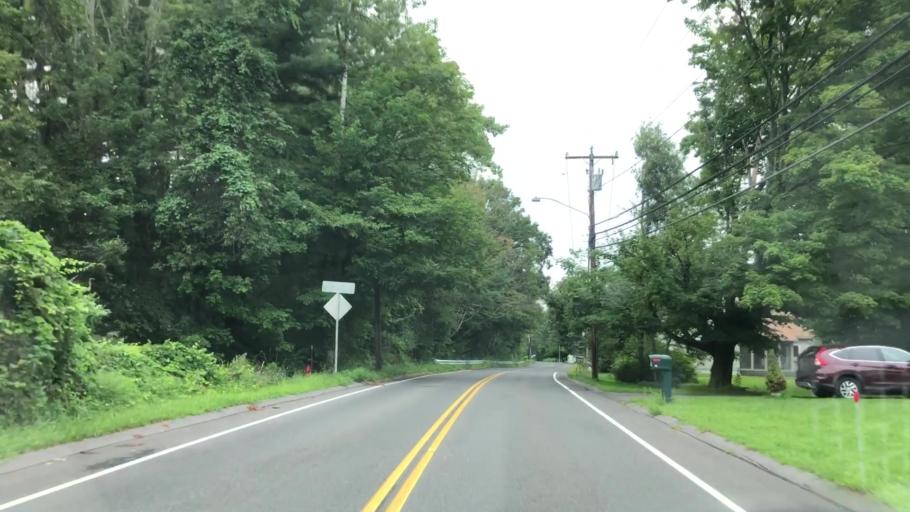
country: US
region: Massachusetts
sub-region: Hampshire County
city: Easthampton
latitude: 42.2694
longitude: -72.6951
